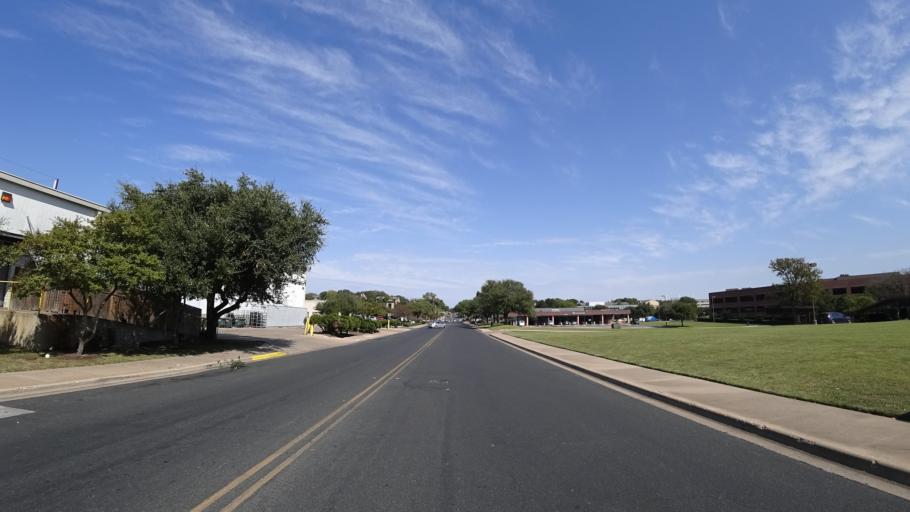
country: US
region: Texas
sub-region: Travis County
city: West Lake Hills
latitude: 30.3514
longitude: -97.7544
